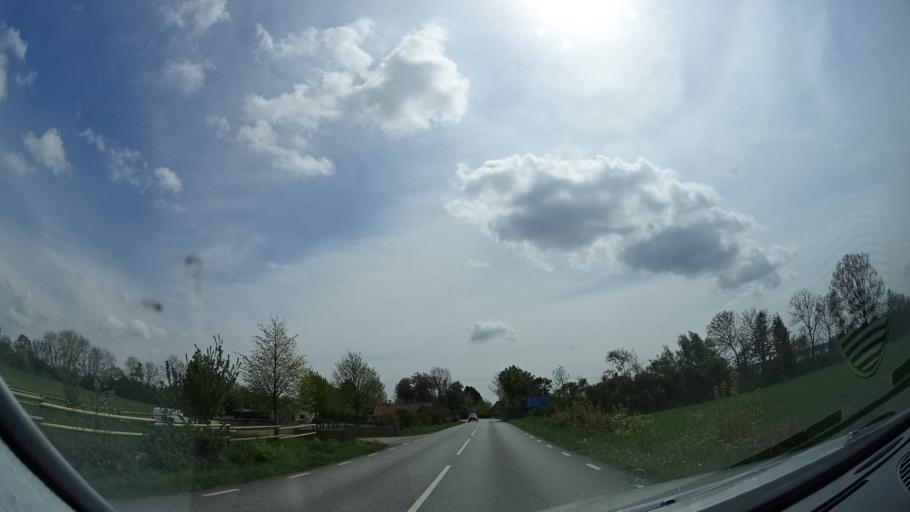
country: SE
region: Skane
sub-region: Hoors Kommun
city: Loberod
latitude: 55.7071
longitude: 13.5580
